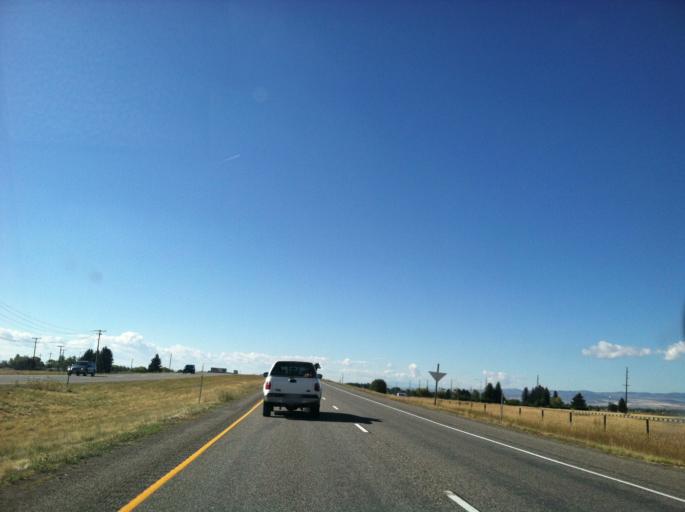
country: US
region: Montana
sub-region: Gallatin County
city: Bozeman
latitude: 45.7283
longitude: -111.0874
